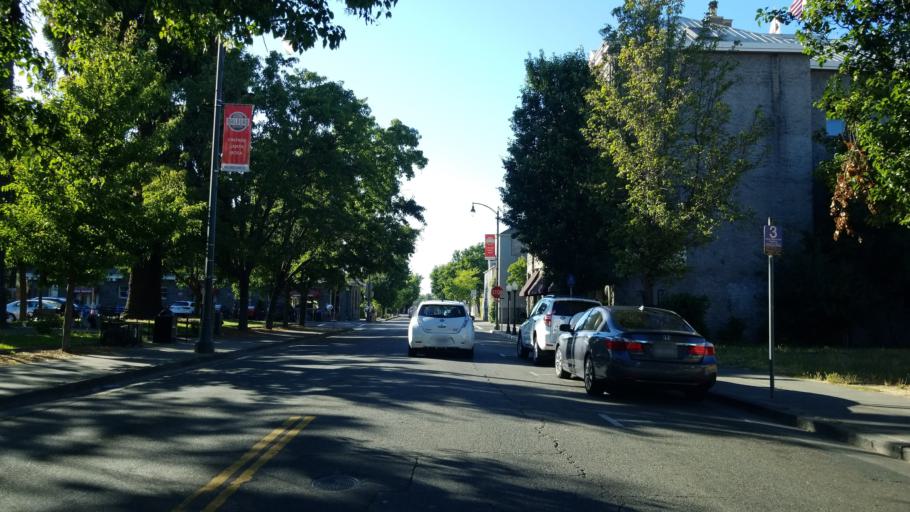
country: US
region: California
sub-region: Sonoma County
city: Santa Rosa
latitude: 38.4376
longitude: -122.7208
